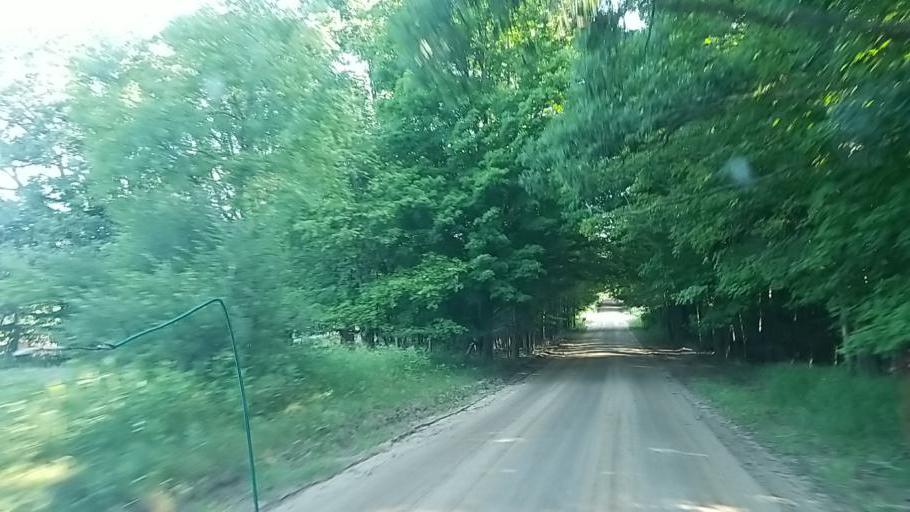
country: US
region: Michigan
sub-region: Newaygo County
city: Newaygo
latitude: 43.3724
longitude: -85.8504
